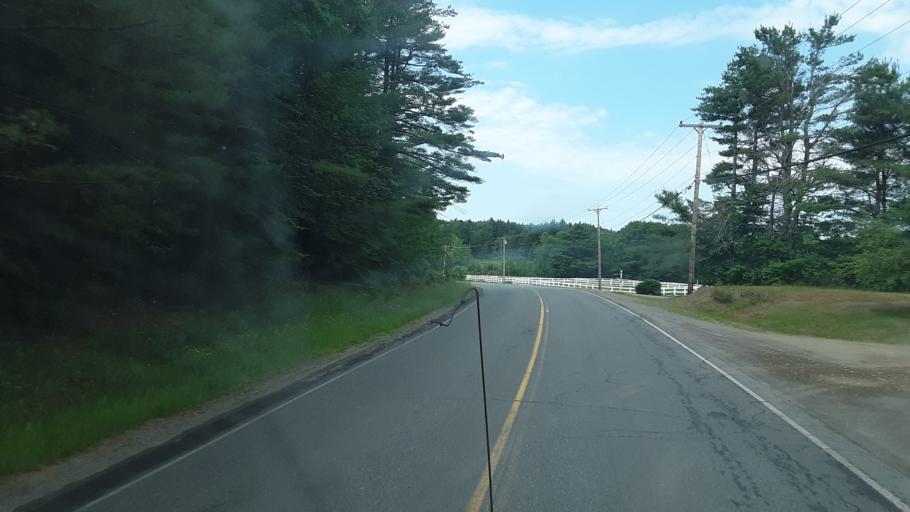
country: US
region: Maine
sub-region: Penobscot County
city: Hampden
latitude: 44.7272
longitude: -68.8766
